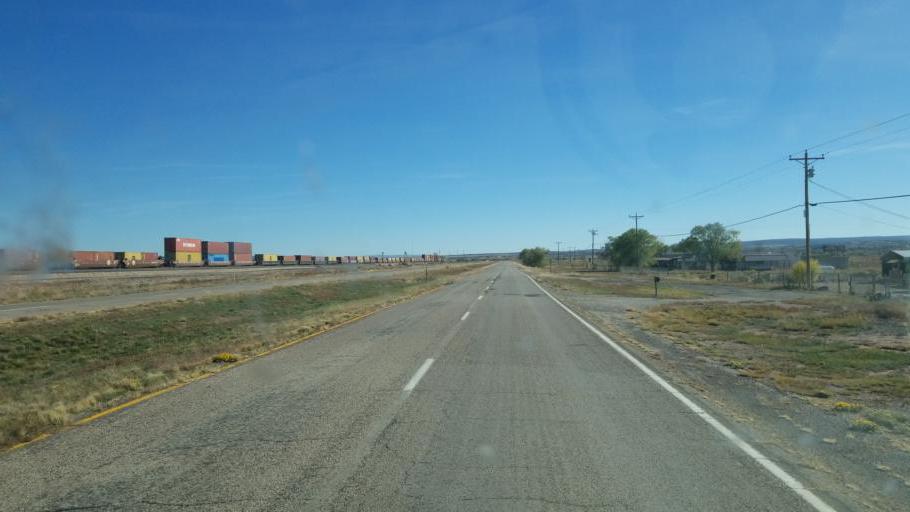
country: US
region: New Mexico
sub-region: Cibola County
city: Milan
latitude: 35.2778
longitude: -107.9820
